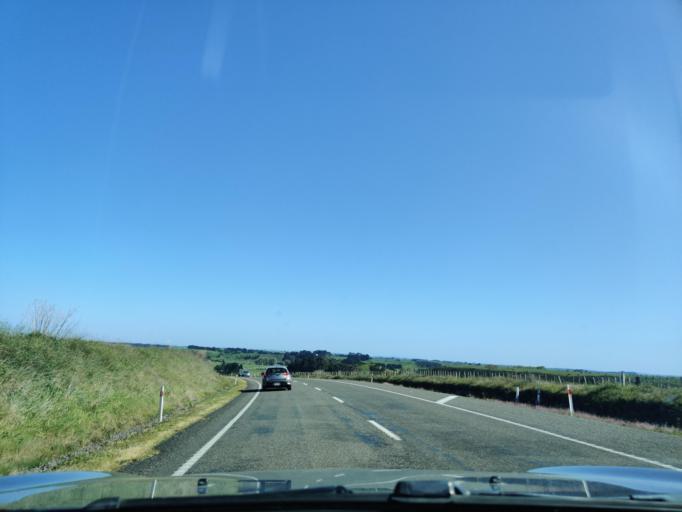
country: NZ
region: Manawatu-Wanganui
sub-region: Rangitikei District
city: Bulls
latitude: -40.0744
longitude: 175.2344
